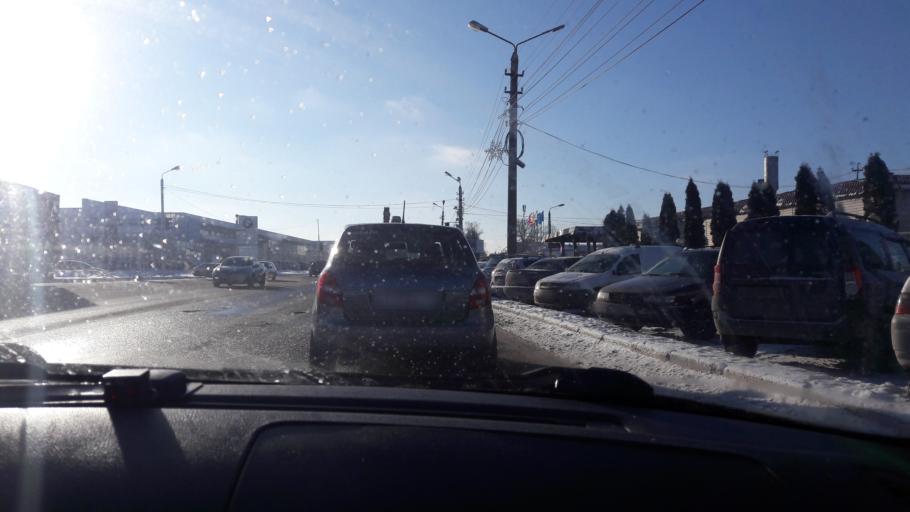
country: RU
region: Tula
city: Tula
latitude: 54.1665
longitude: 37.6413
